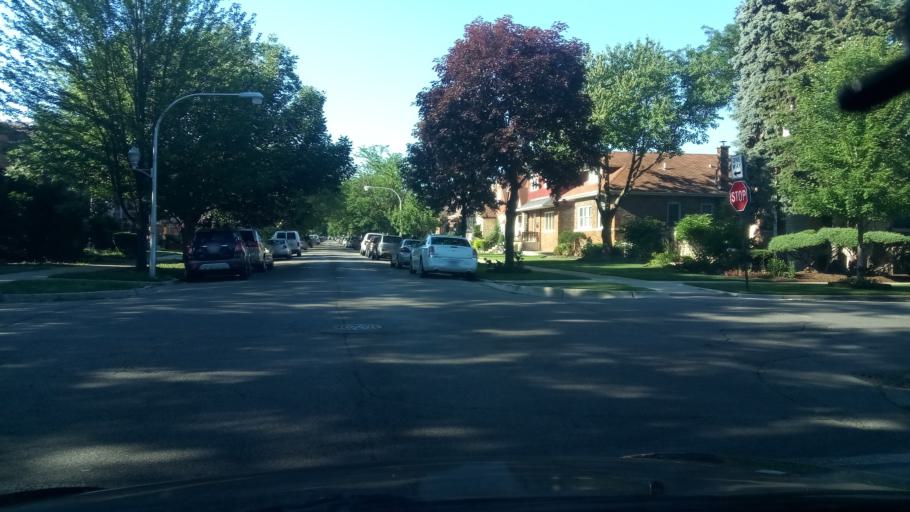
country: US
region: Illinois
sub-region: Cook County
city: Hometown
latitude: 41.7775
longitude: -87.7276
